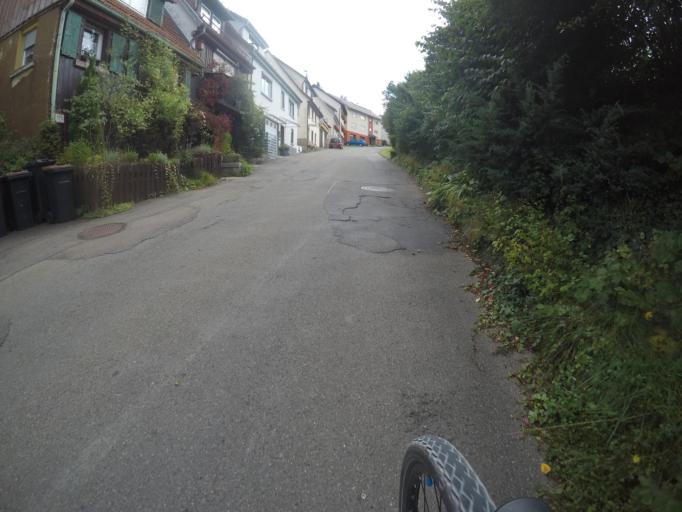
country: DE
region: Baden-Wuerttemberg
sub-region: Tuebingen Region
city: Munsingen
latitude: 48.4306
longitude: 9.4962
